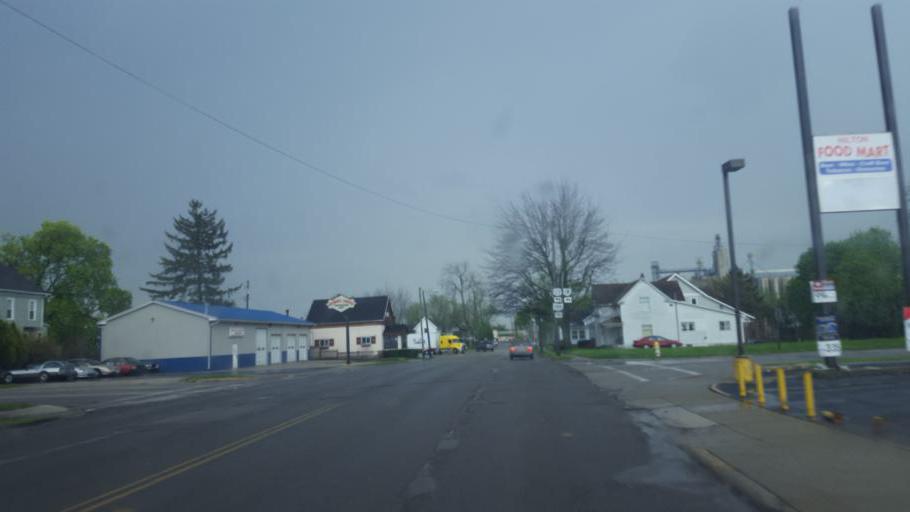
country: US
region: Ohio
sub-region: Seneca County
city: Fostoria
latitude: 41.1569
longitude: -83.4213
